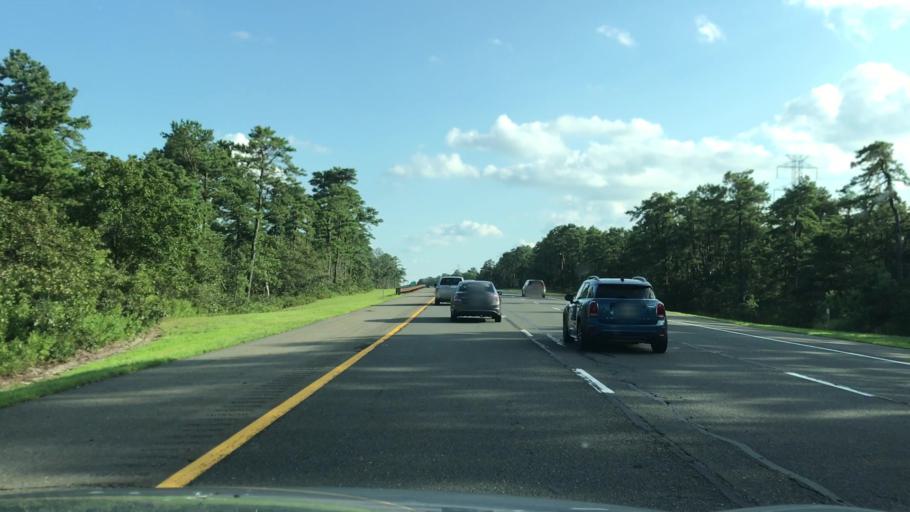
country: US
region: New Jersey
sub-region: Ocean County
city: Forked River
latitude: 39.8289
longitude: -74.2274
